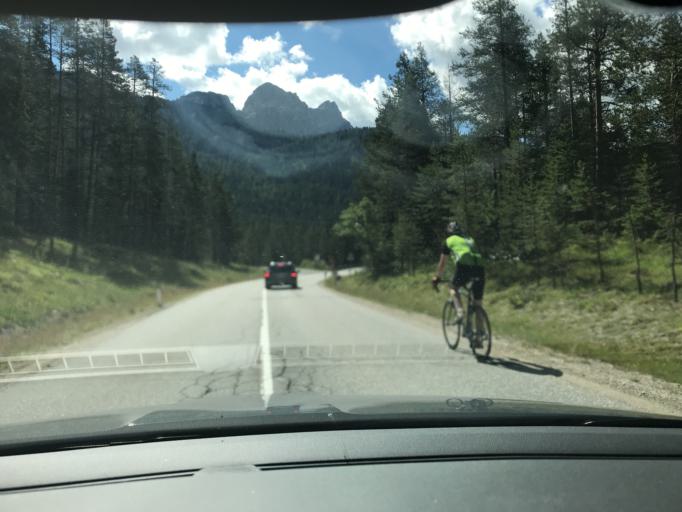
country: IT
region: Veneto
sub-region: Provincia di Belluno
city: Livinallongo del Col di Lana
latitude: 46.5564
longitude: 11.9649
